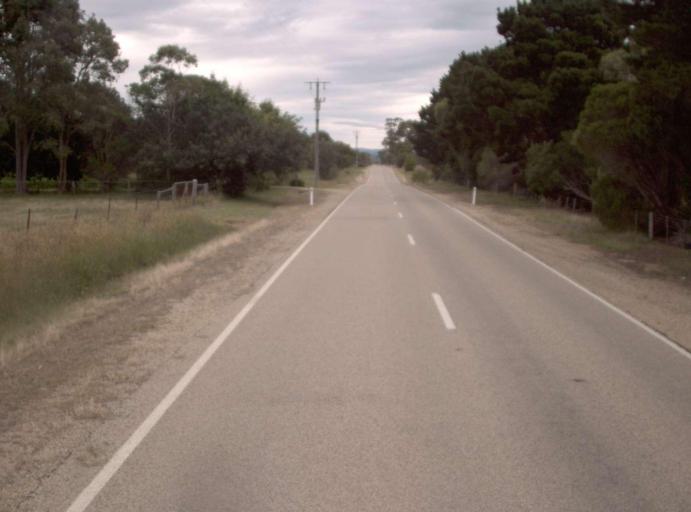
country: AU
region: Victoria
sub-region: East Gippsland
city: Bairnsdale
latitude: -37.8578
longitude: 147.5640
